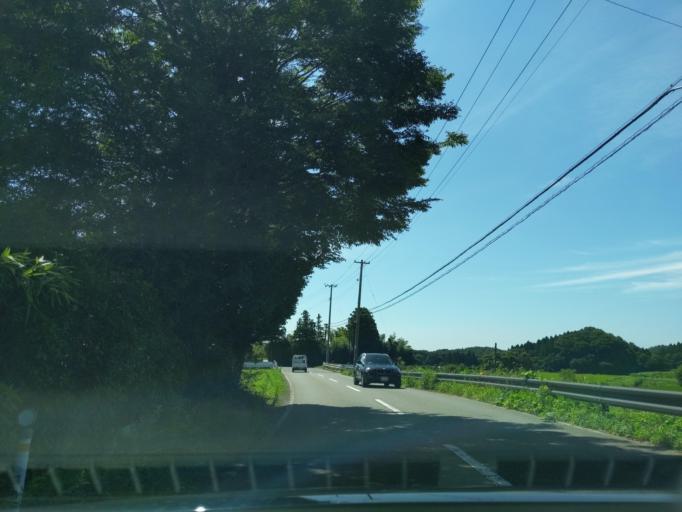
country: JP
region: Fukushima
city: Koriyama
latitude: 37.3829
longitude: 140.2614
